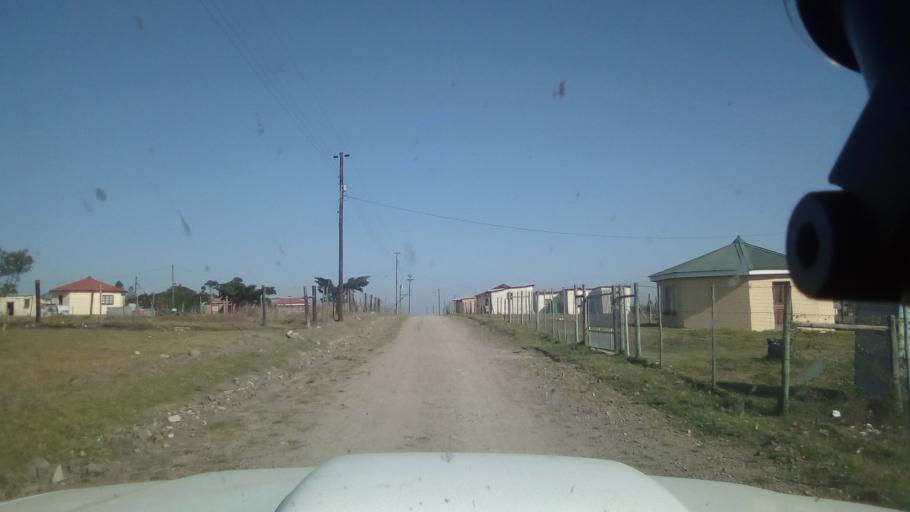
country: ZA
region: Eastern Cape
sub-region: Buffalo City Metropolitan Municipality
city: Bhisho
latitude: -32.9406
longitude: 27.3378
